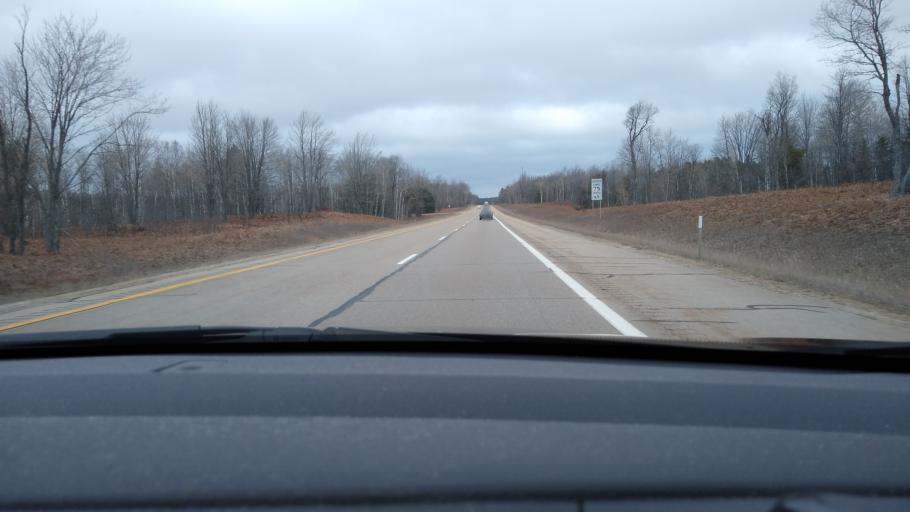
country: US
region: Michigan
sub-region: Crawford County
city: Grayling
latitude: 44.7957
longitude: -84.7136
